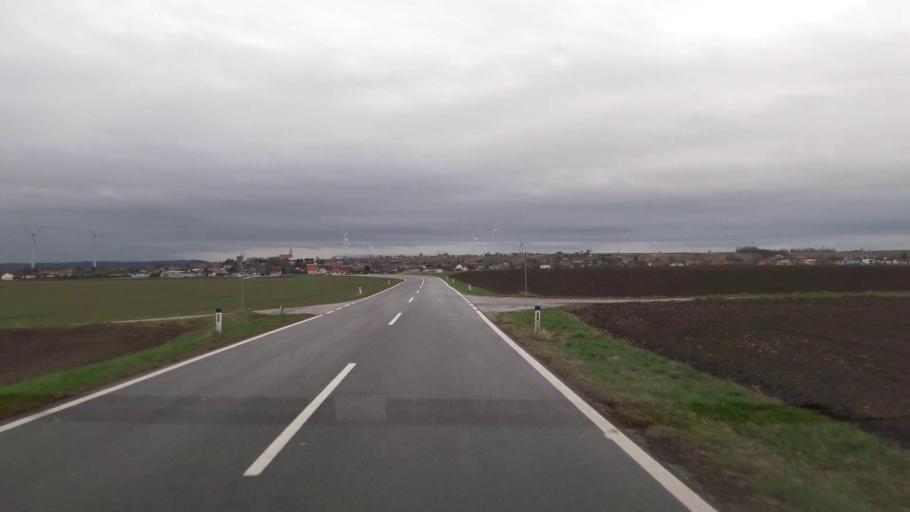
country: AT
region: Lower Austria
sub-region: Politischer Bezirk Bruck an der Leitha
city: Scharndorf
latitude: 48.0789
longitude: 16.7943
